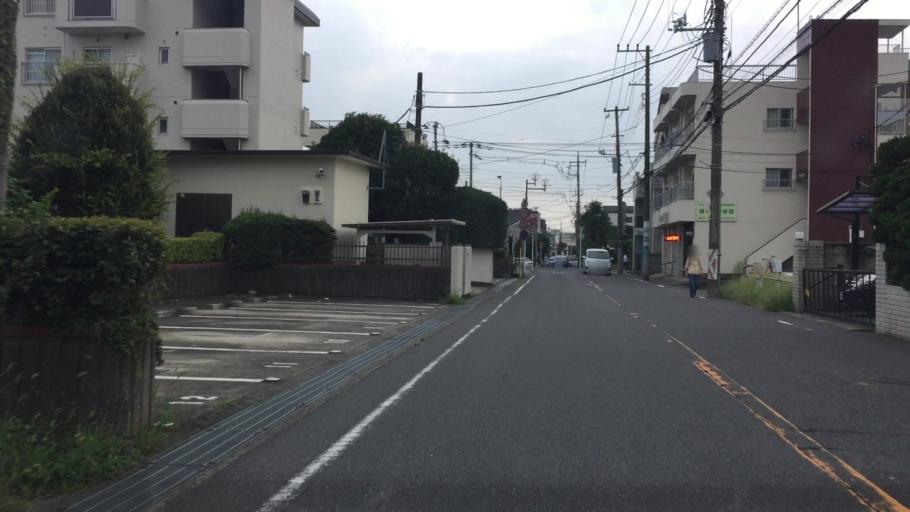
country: JP
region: Chiba
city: Matsudo
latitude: 35.7849
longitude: 139.9107
